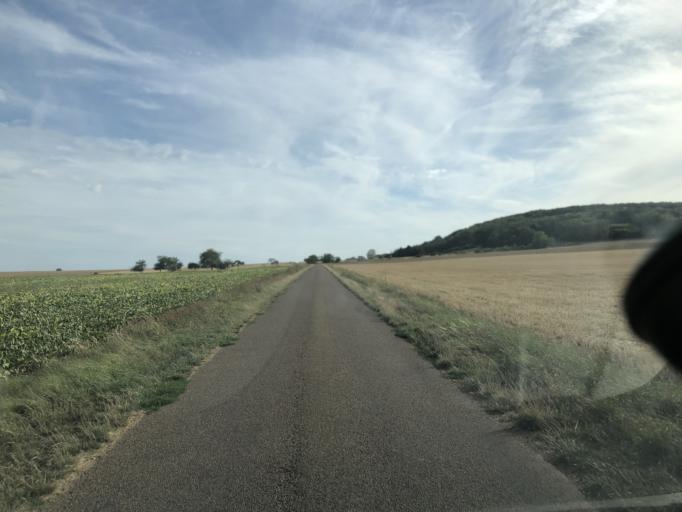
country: FR
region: Bourgogne
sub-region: Departement de l'Yonne
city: Joigny
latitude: 47.9486
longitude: 3.3947
